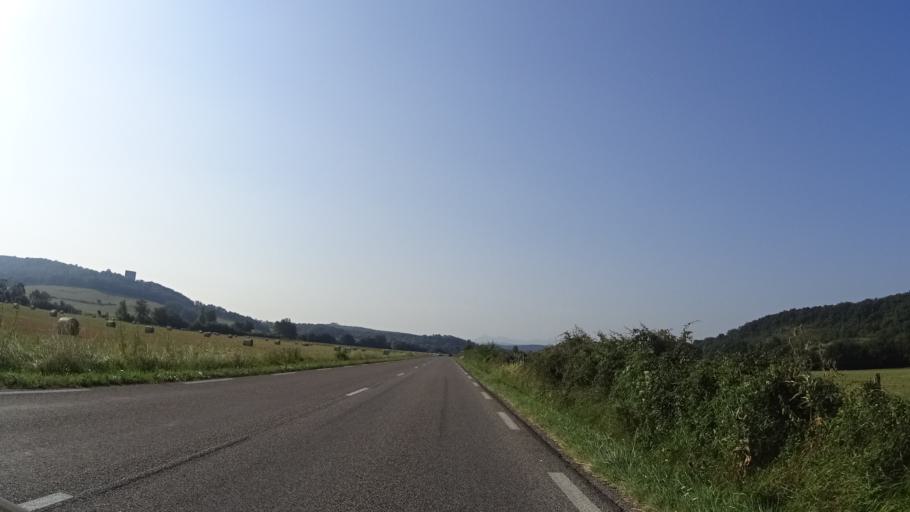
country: FR
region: Midi-Pyrenees
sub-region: Departement de l'Ariege
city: Mirepoix
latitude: 43.0439
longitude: 1.8955
